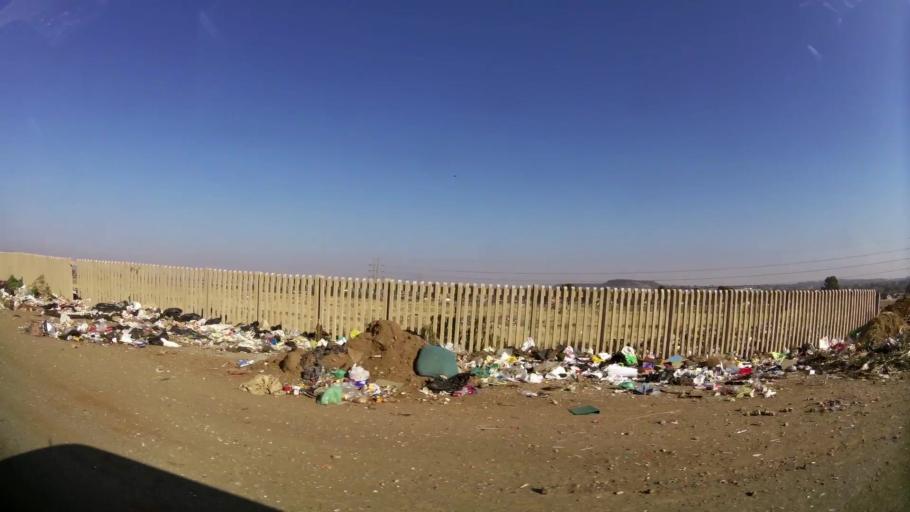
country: ZA
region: Orange Free State
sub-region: Mangaung Metropolitan Municipality
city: Bloemfontein
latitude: -29.1756
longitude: 26.1958
